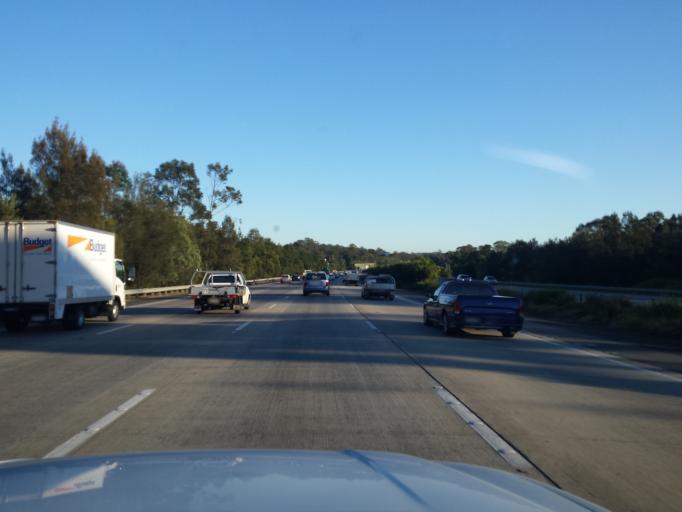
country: AU
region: Queensland
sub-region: Gold Coast
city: Ormeau Hills
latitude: -27.8029
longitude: 153.2633
